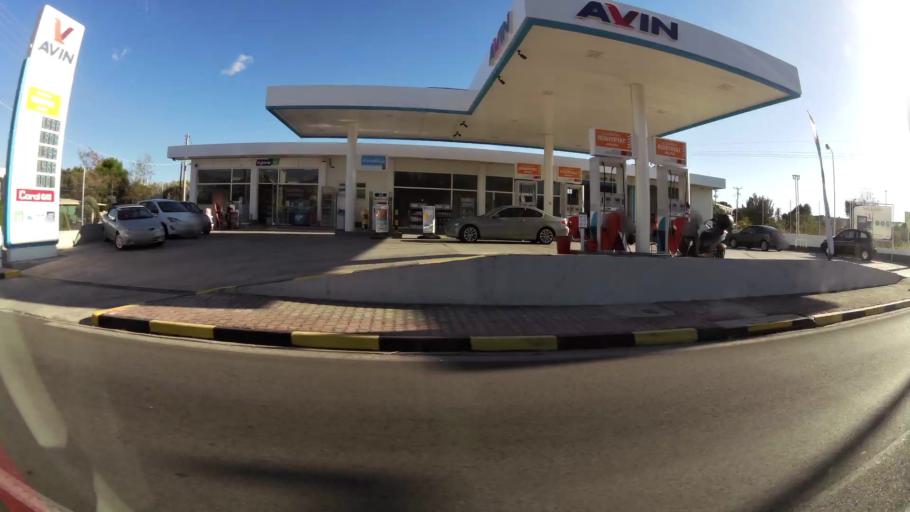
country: GR
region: Attica
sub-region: Nomarchia Anatolikis Attikis
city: Pikermi
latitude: 38.0010
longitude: 23.9379
